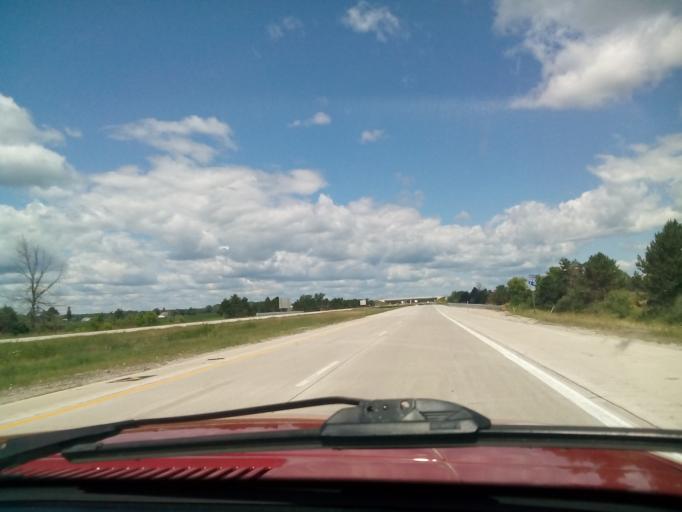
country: US
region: Michigan
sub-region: Bay County
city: Pinconning
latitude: 43.8618
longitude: -84.0205
